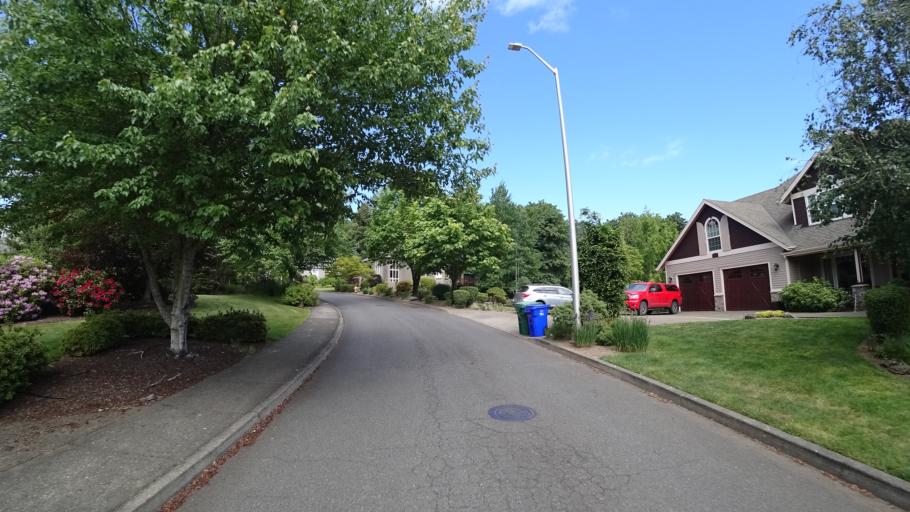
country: US
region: Oregon
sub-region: Washington County
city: Oak Hills
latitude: 45.5927
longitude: -122.8252
